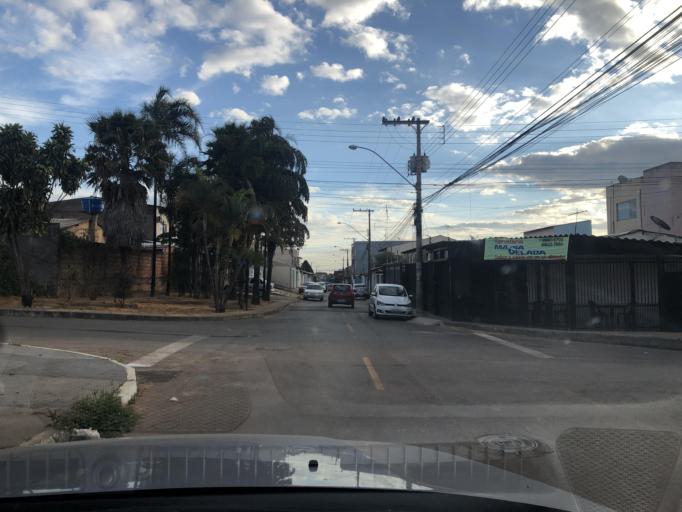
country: BR
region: Federal District
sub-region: Brasilia
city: Brasilia
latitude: -15.8687
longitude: -48.0948
